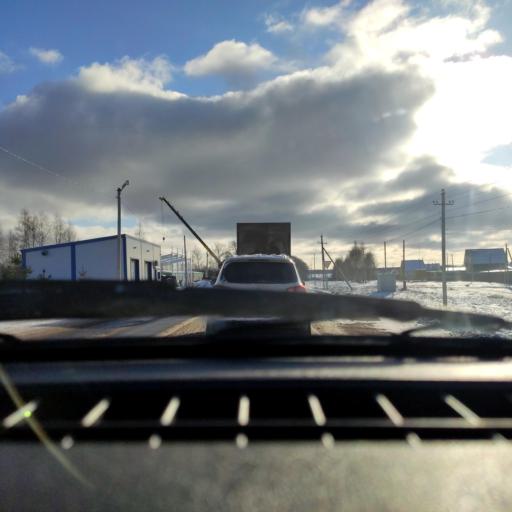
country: RU
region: Bashkortostan
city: Iglino
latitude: 54.8128
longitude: 56.4081
